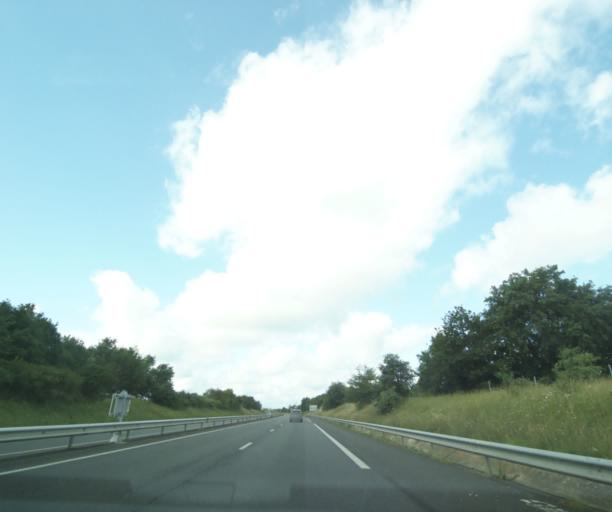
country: FR
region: Pays de la Loire
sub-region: Departement de la Sarthe
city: Vion
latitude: 47.7737
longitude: -0.2158
